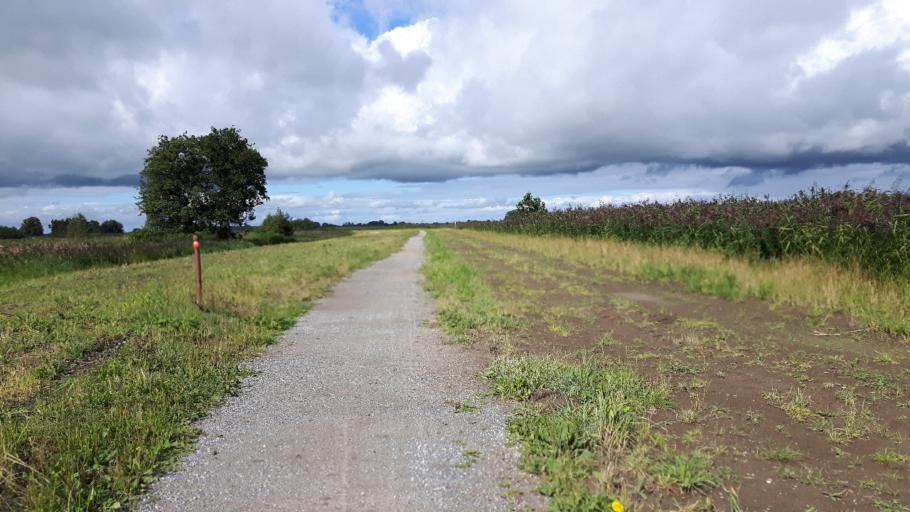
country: NL
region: Groningen
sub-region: Gemeente Slochteren
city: Slochteren
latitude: 53.2675
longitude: 6.8215
